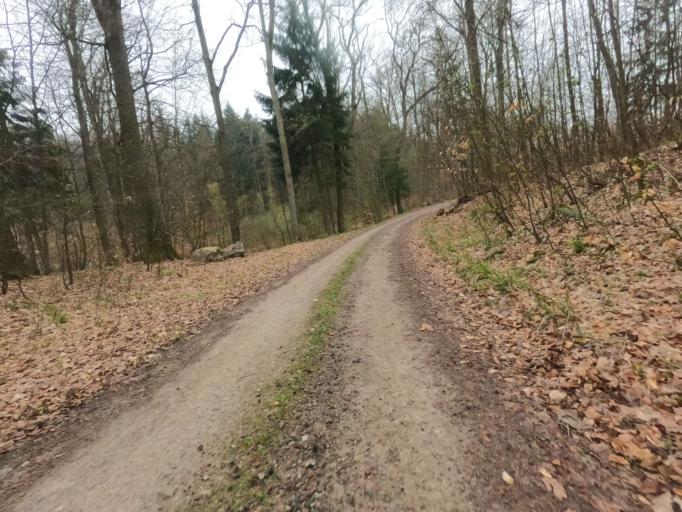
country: PL
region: West Pomeranian Voivodeship
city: Trzcinsko Zdroj
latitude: 52.9259
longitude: 14.7049
